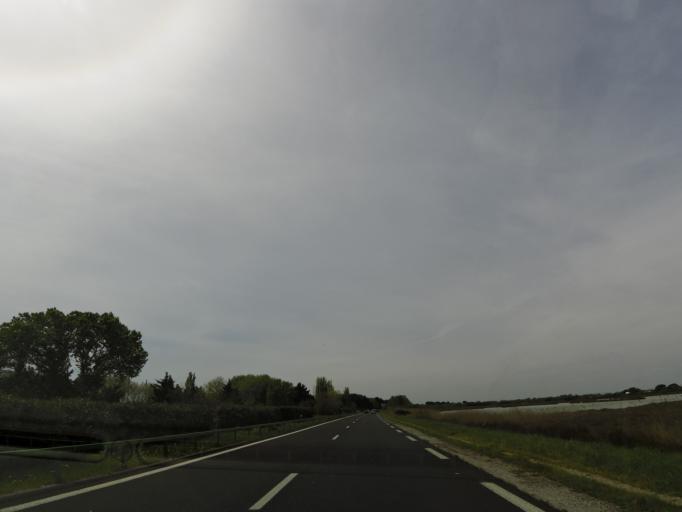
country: FR
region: Languedoc-Roussillon
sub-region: Departement de l'Herault
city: La Grande-Motte
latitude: 43.5742
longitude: 4.0899
